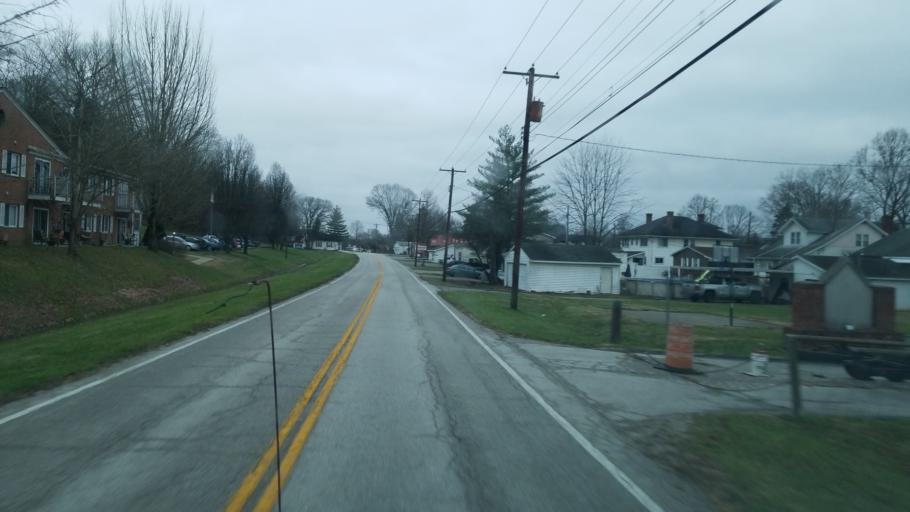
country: US
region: Kentucky
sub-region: Bracken County
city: Augusta
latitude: 38.7713
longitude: -83.9984
